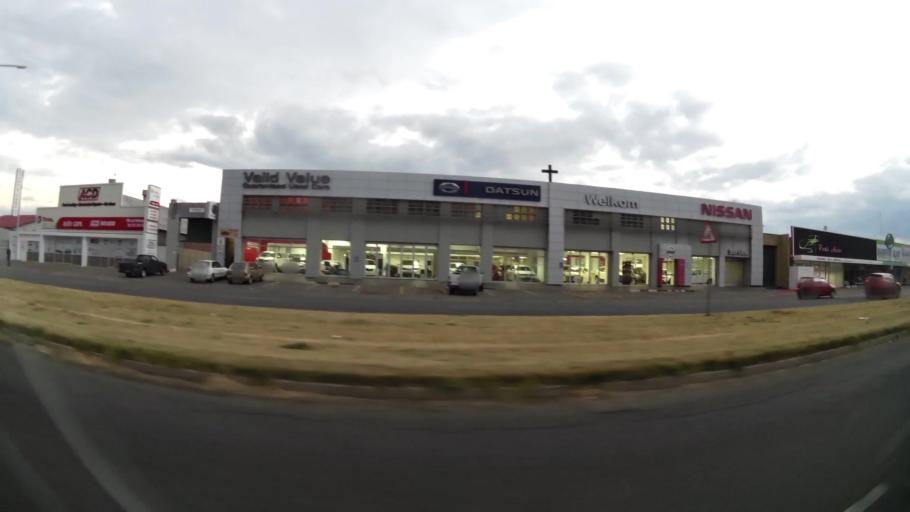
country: ZA
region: Orange Free State
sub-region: Lejweleputswa District Municipality
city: Welkom
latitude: -27.9812
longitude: 26.7646
